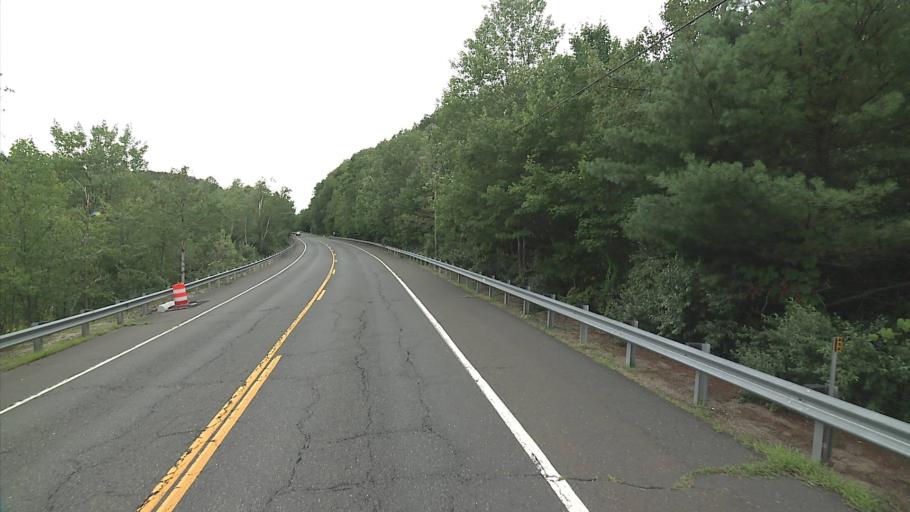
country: US
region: Connecticut
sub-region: Litchfield County
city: Winsted
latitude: 42.0086
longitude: -73.0493
